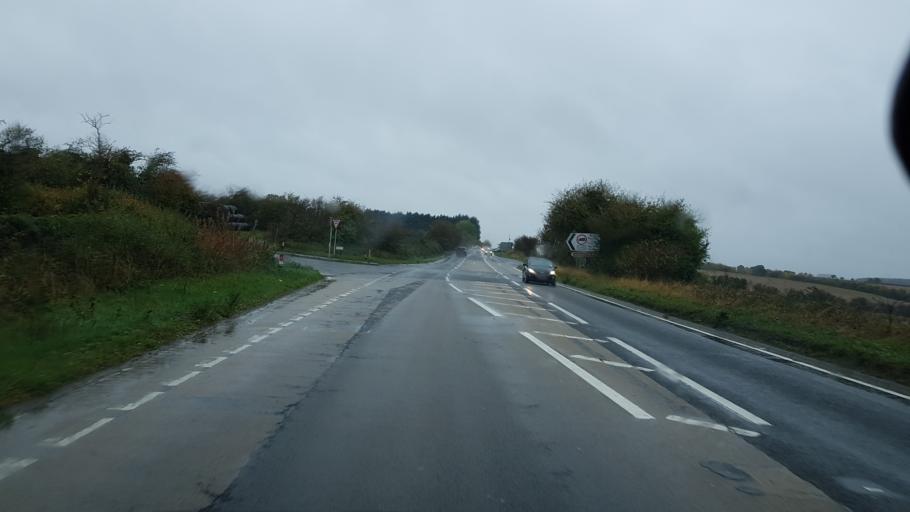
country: GB
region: England
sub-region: Oxfordshire
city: Carterton
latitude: 51.7922
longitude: -1.5968
